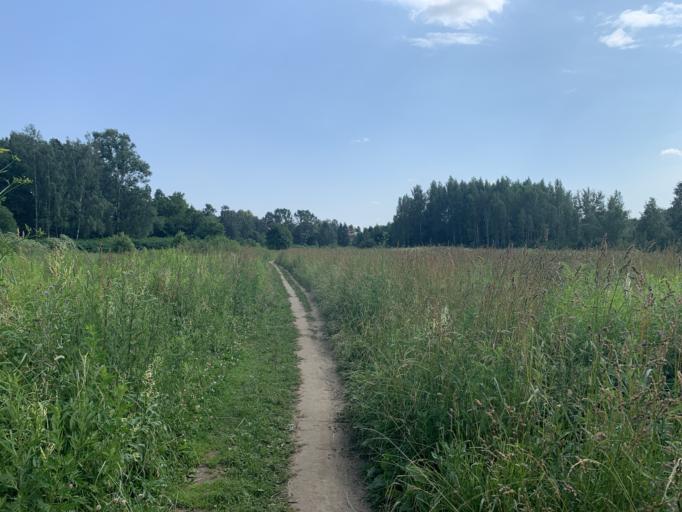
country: RU
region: Moskovskaya
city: Cherkizovo
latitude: 55.9725
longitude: 37.7950
